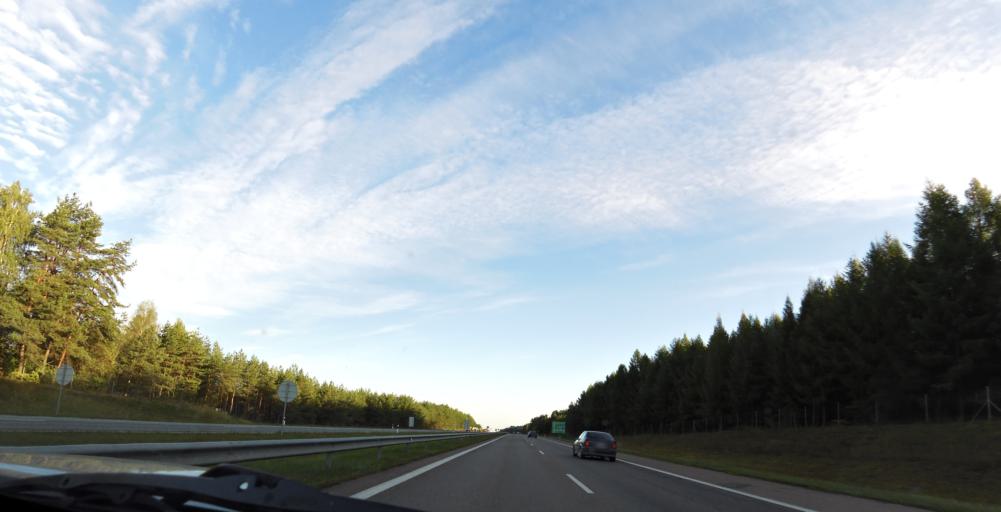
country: LT
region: Vilnius County
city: Ukmerge
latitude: 55.2625
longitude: 24.8139
